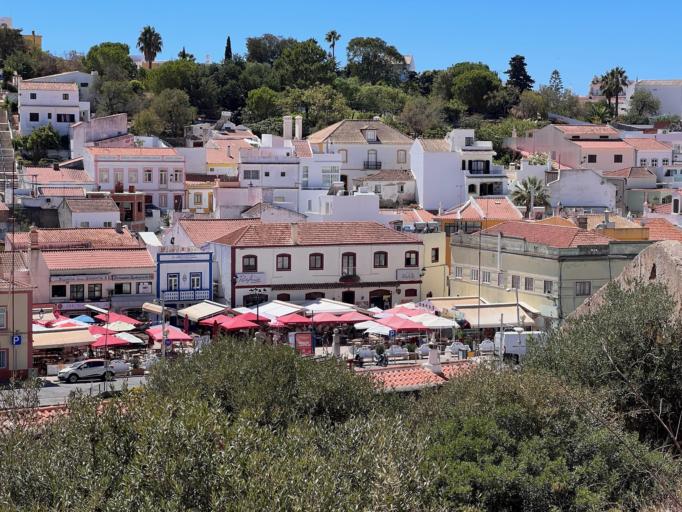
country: PT
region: Faro
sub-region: Portimao
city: Portimao
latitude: 37.1260
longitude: -8.5195
